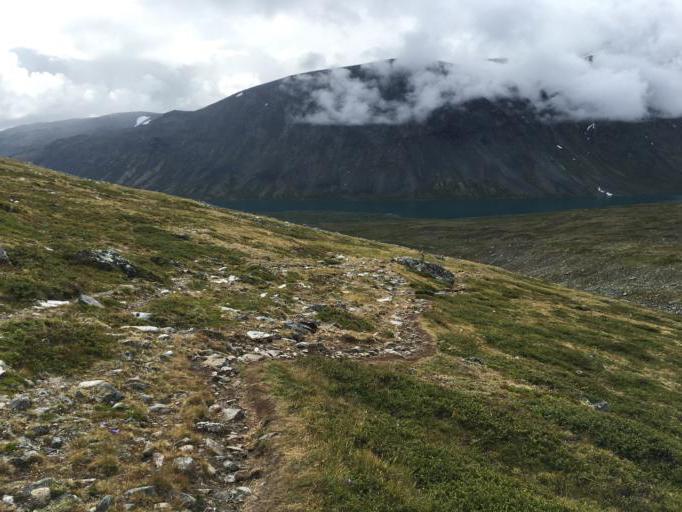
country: NO
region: Oppland
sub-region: Lom
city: Fossbergom
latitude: 61.5725
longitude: 8.6729
